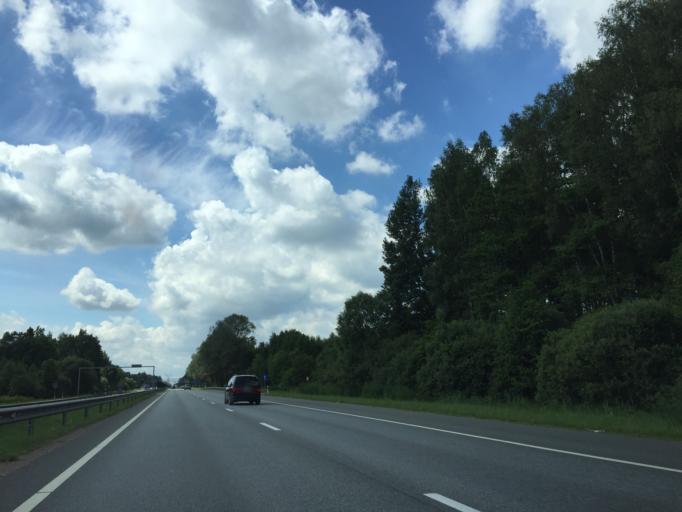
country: LV
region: Olaine
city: Olaine
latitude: 56.7468
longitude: 23.8863
